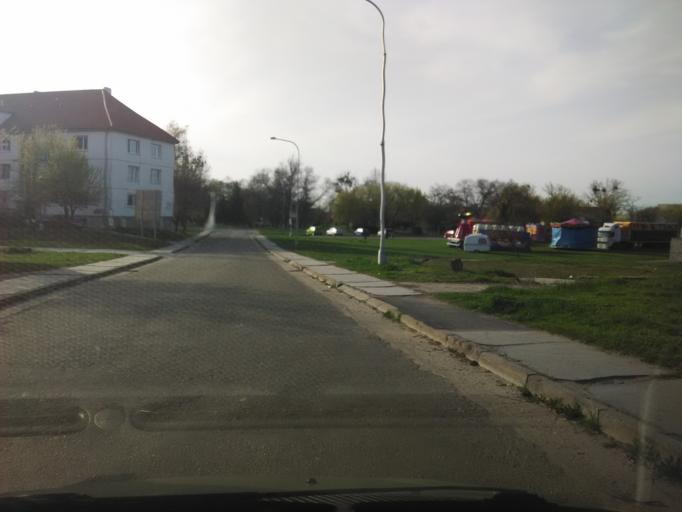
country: SK
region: Nitriansky
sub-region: Okres Nove Zamky
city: Nove Zamky
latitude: 47.9877
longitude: 18.1609
